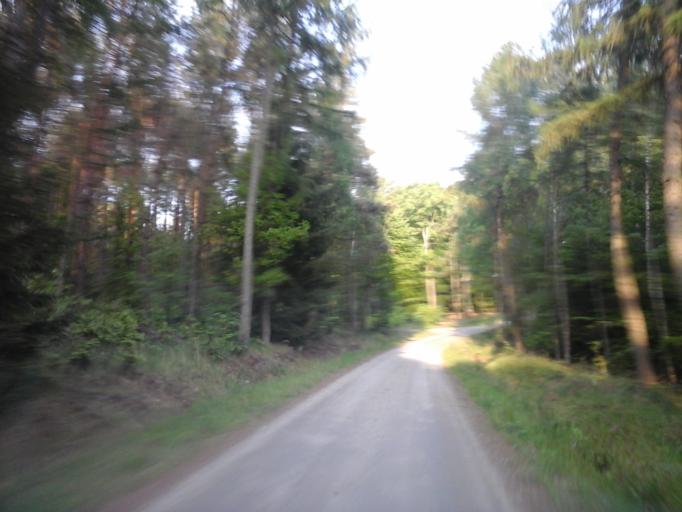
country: PL
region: West Pomeranian Voivodeship
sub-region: Powiat choszczenski
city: Krzecin
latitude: 52.9953
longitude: 15.4675
